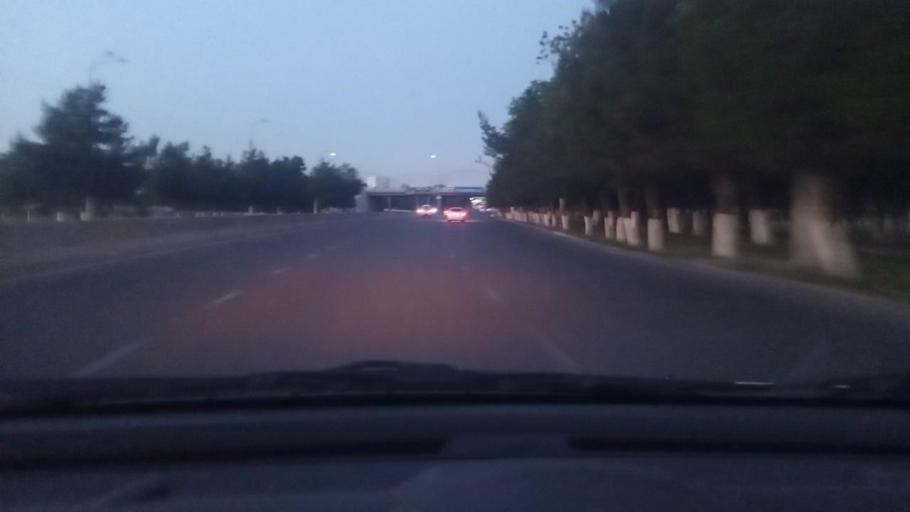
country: UZ
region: Toshkent Shahri
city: Tashkent
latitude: 41.2457
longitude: 69.2181
